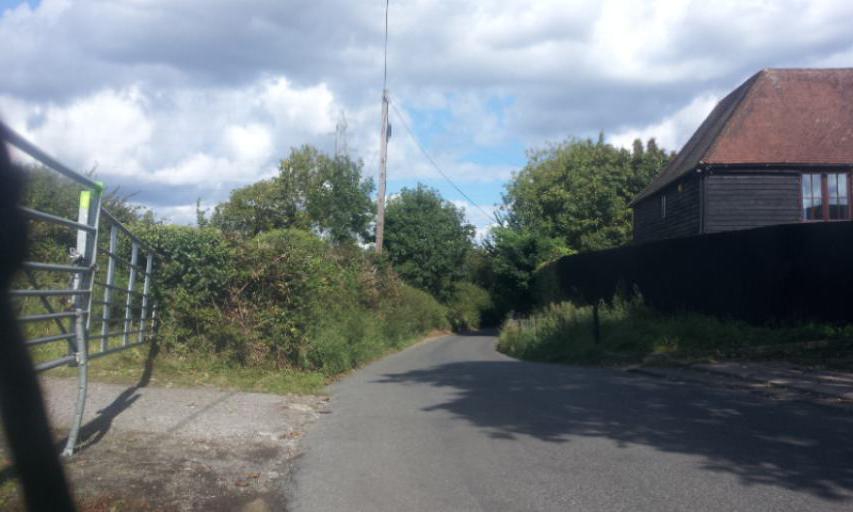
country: GB
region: England
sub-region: Kent
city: Snodland
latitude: 51.3243
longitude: 0.4259
